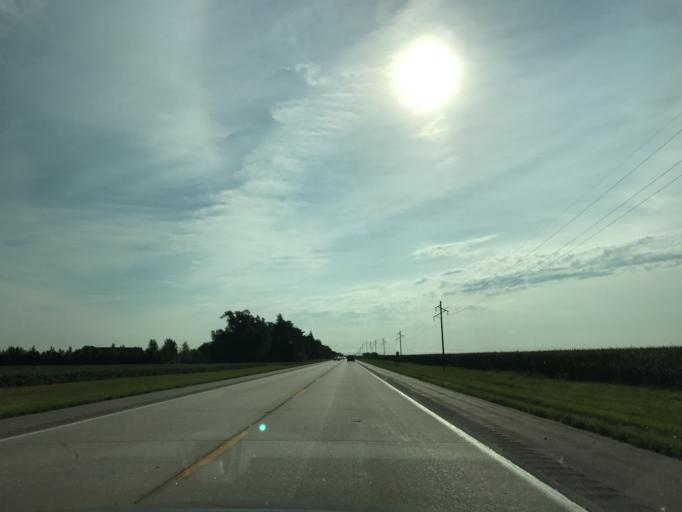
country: US
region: Nebraska
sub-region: Polk County
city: Osceola
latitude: 41.1921
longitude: -97.3377
